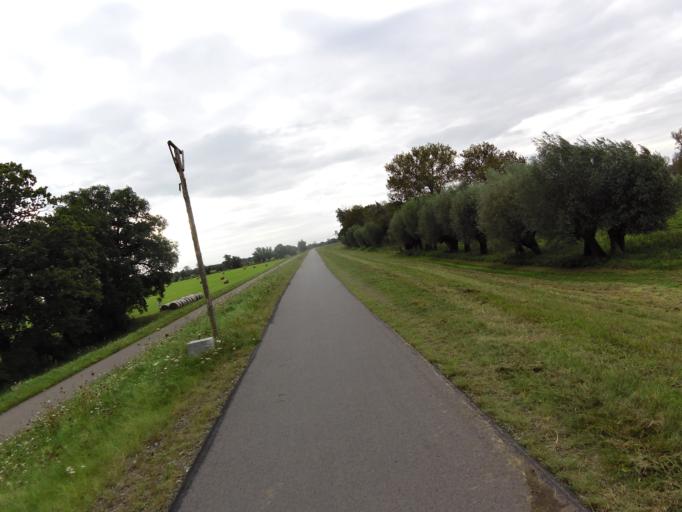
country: DE
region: Brandenburg
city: Breese
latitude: 52.9794
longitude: 11.7735
